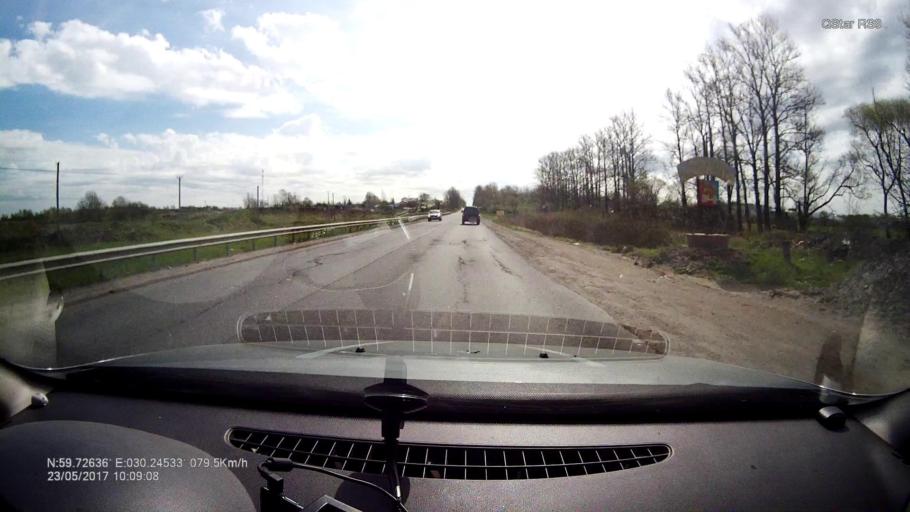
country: RU
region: St.-Petersburg
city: Aleksandrovskaya
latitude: 59.7262
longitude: 30.2453
